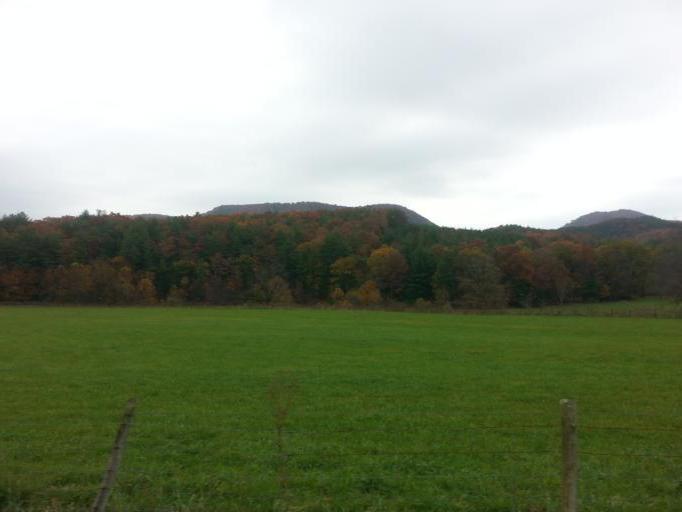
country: US
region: Virginia
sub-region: Pulaski County
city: Pulaski
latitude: 37.1058
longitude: -80.8934
